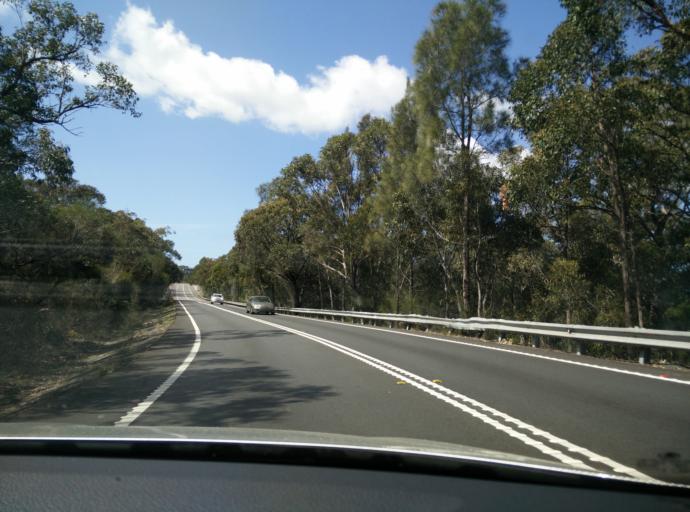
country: AU
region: New South Wales
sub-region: Gosford Shire
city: Point Clare
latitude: -33.4623
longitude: 151.2815
